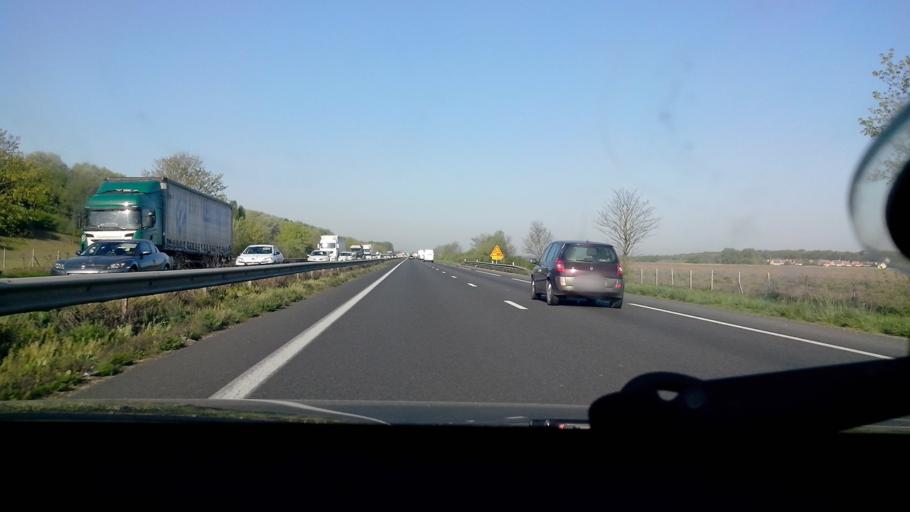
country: FR
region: Ile-de-France
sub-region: Departement de Seine-et-Marne
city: Moissy-Cramayel
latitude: 48.6464
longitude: 2.5948
